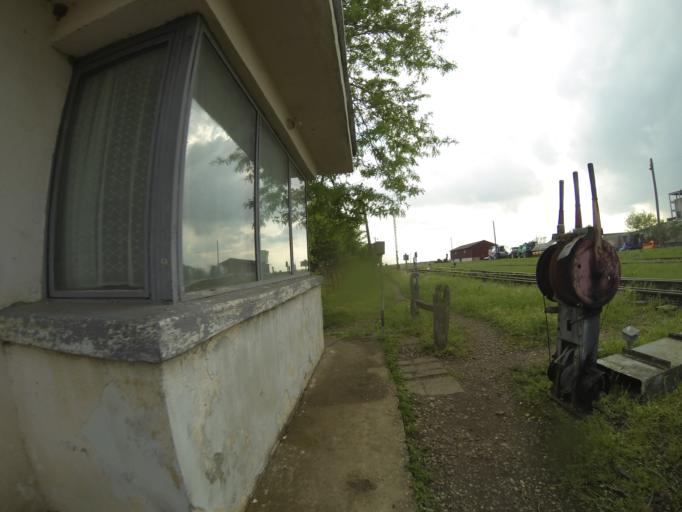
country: RO
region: Dolj
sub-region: Comuna Segarcea
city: Segarcea
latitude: 44.0828
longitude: 23.7272
